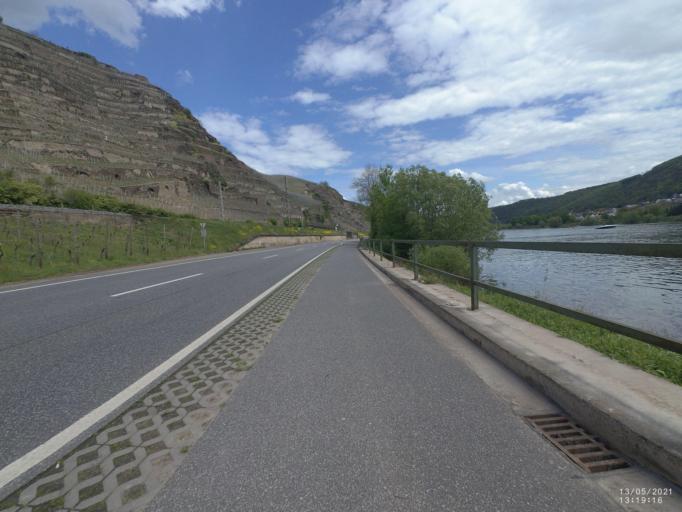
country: DE
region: Rheinland-Pfalz
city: Winningen
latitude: 50.3210
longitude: 7.5294
